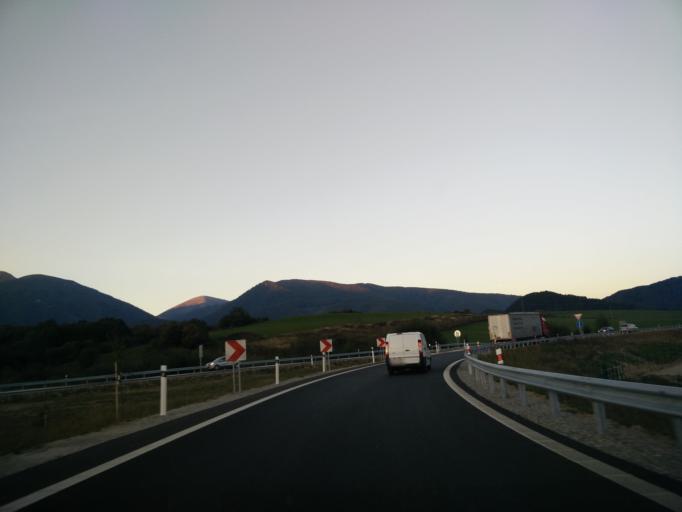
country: SK
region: Zilinsky
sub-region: Okres Zilina
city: Terchova
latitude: 49.1318
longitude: 19.0724
